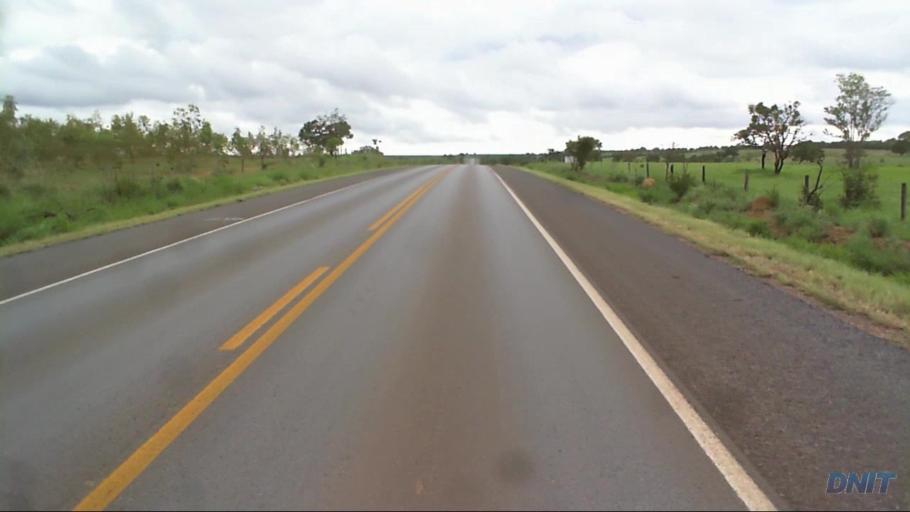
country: BR
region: Goias
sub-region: Barro Alto
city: Barro Alto
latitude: -15.2130
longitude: -48.6630
